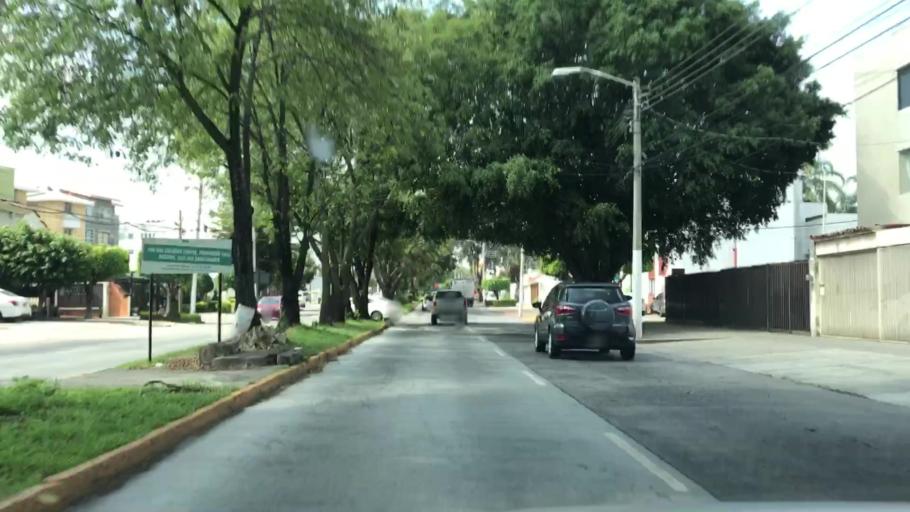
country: MX
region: Jalisco
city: Guadalajara
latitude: 20.6604
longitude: -103.4100
